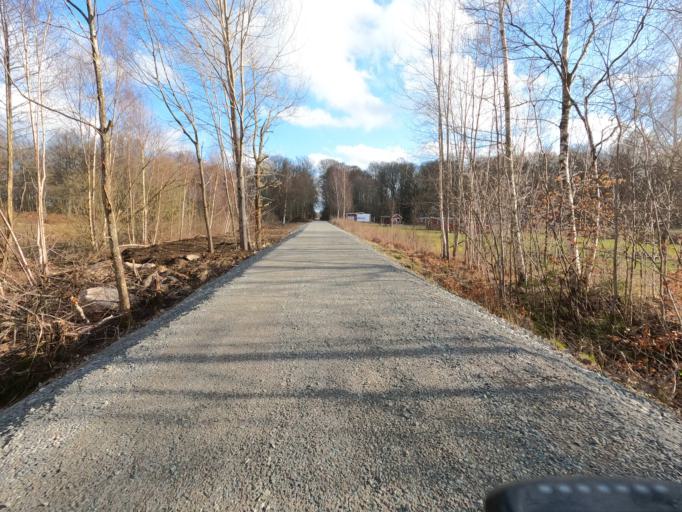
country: SE
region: Kronoberg
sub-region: Vaxjo Kommun
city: Gemla
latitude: 56.6969
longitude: 14.6004
